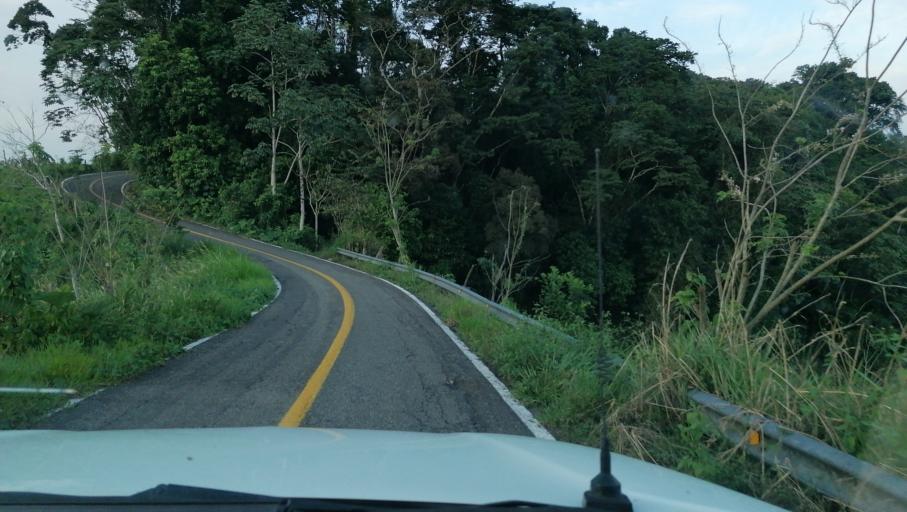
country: MX
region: Chiapas
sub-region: Juarez
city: El Triunfo 1ra. Seccion (Cardona)
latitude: 17.5030
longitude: -93.2363
